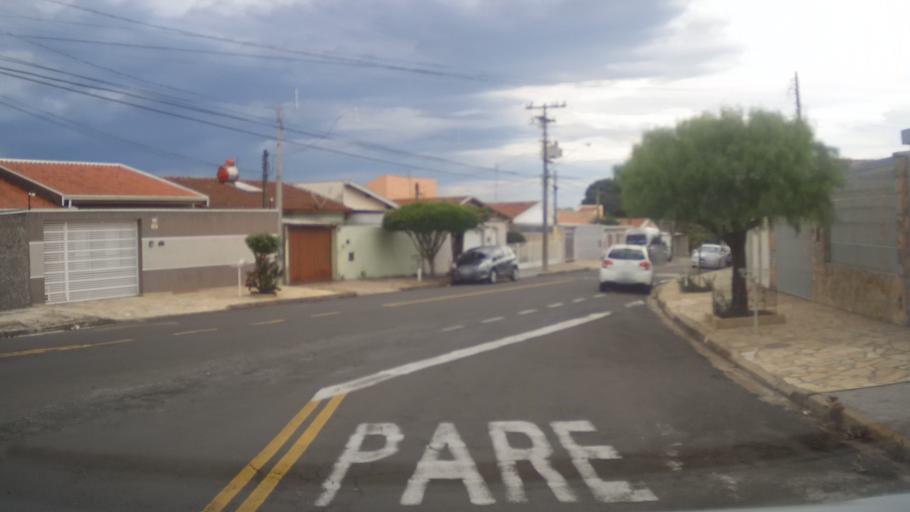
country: BR
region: Sao Paulo
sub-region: Campinas
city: Campinas
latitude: -22.8911
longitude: -47.1072
